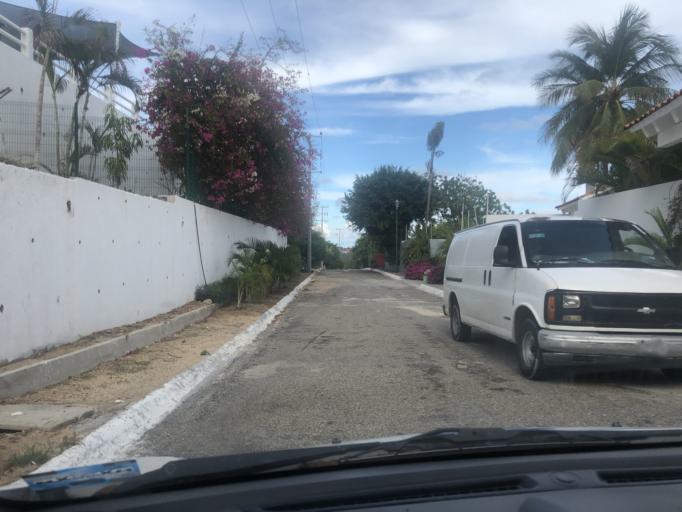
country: MX
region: Oaxaca
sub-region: Santa Maria Huatulco
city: Crucecita
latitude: 15.7718
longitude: -96.0884
